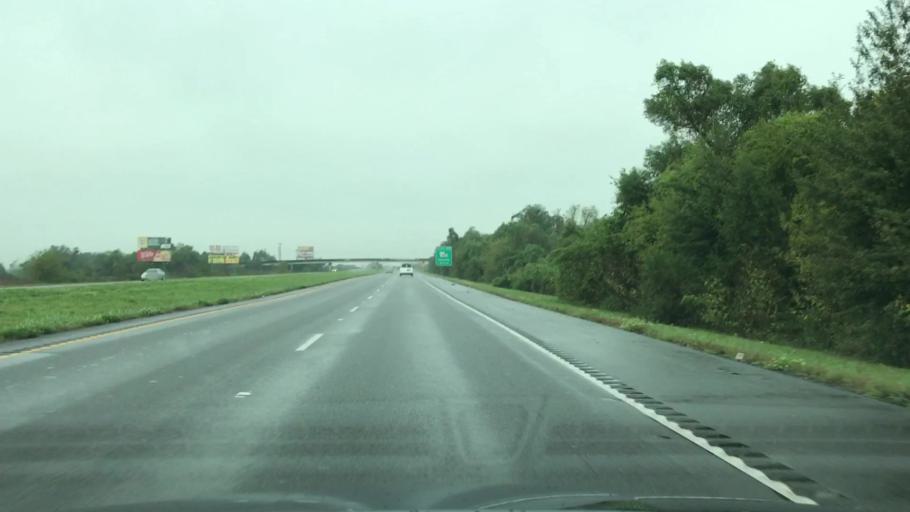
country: US
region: Louisiana
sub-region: Lafourche Parish
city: Raceland
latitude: 29.6904
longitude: -90.5974
